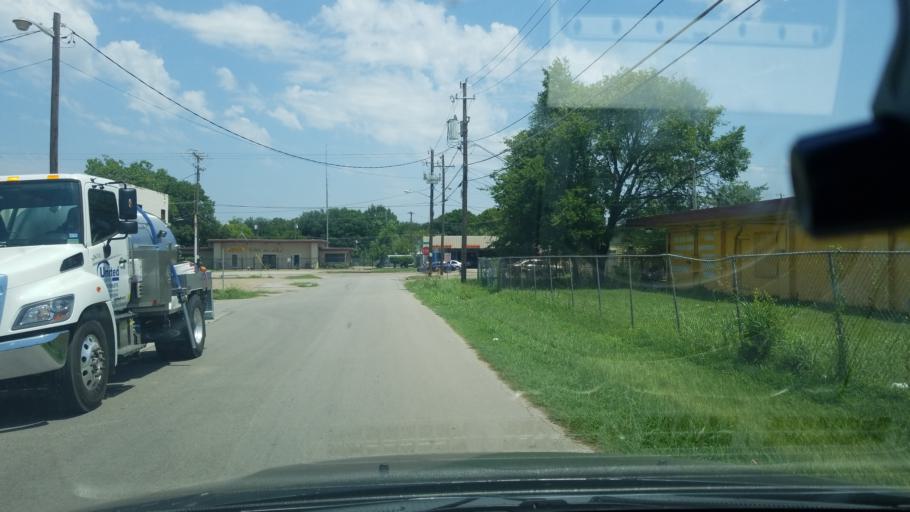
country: US
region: Texas
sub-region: Dallas County
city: Balch Springs
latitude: 32.7334
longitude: -96.6847
